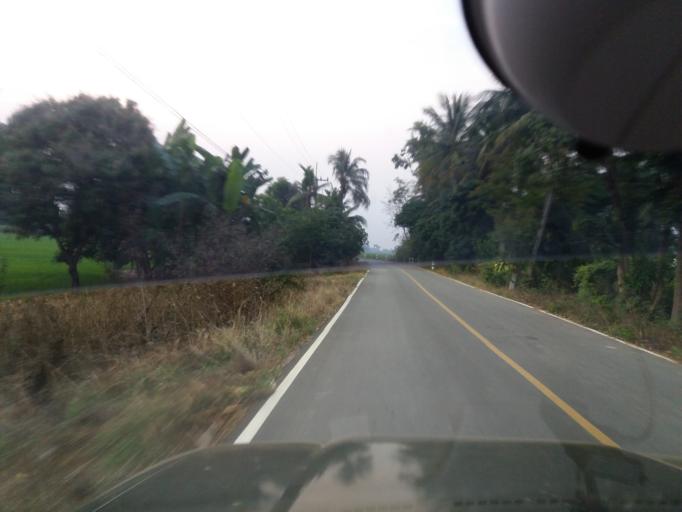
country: TH
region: Suphan Buri
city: Doem Bang Nang Buat
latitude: 14.8931
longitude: 100.1829
